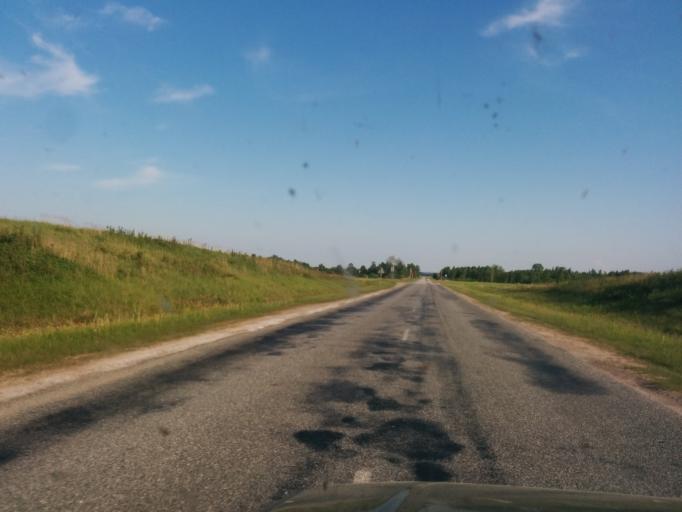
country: LV
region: Talsu Rajons
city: Valdemarpils
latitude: 57.3325
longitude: 22.5155
